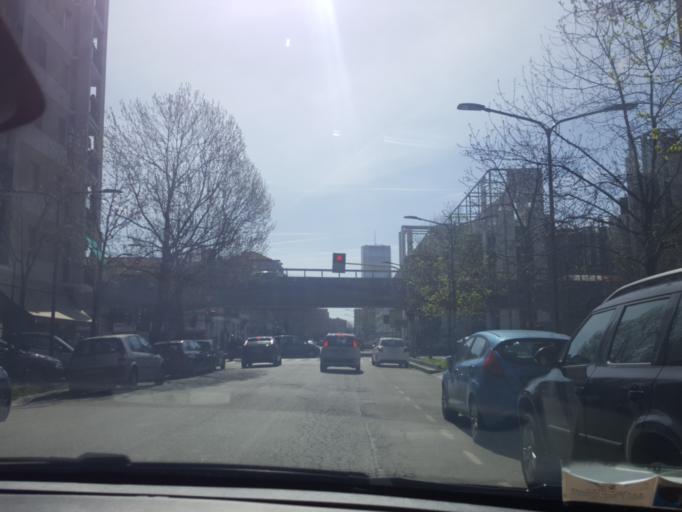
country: IT
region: Lombardy
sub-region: Citta metropolitana di Milano
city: Novate Milanese
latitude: 45.4891
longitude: 9.1487
